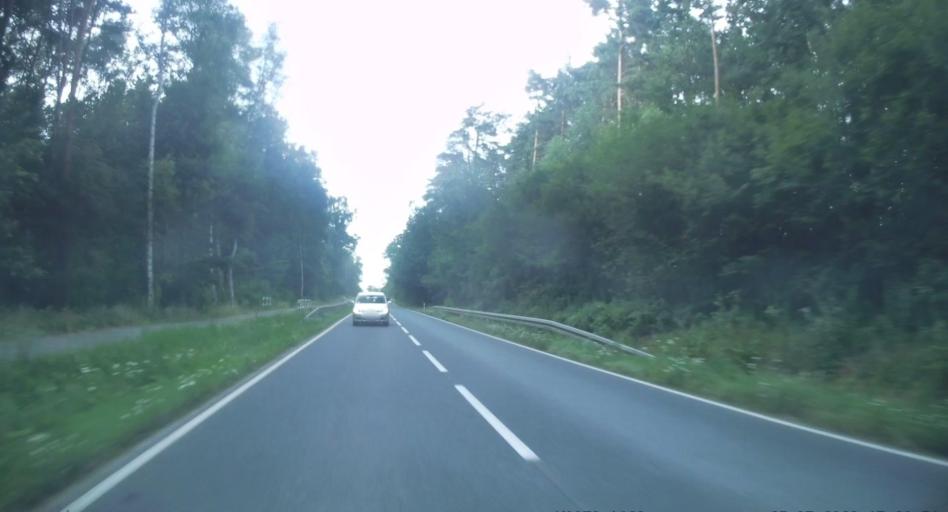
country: PL
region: Lesser Poland Voivodeship
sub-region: Powiat brzeski
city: Przyborow
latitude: 50.0537
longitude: 20.6391
